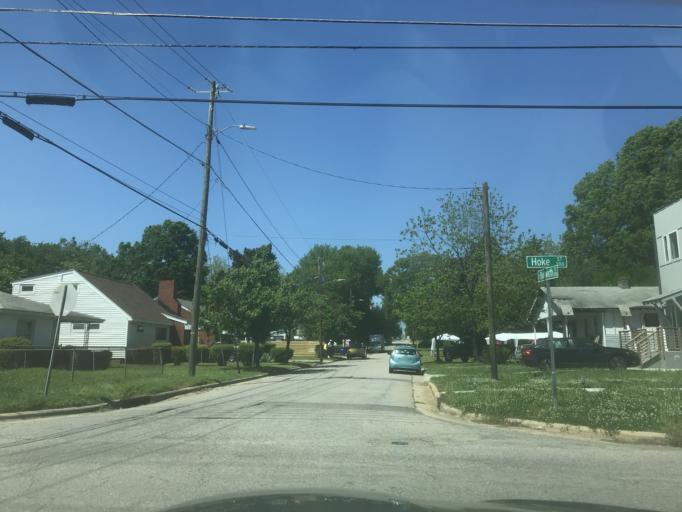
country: US
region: North Carolina
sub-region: Wake County
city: Raleigh
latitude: 35.7634
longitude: -78.6341
